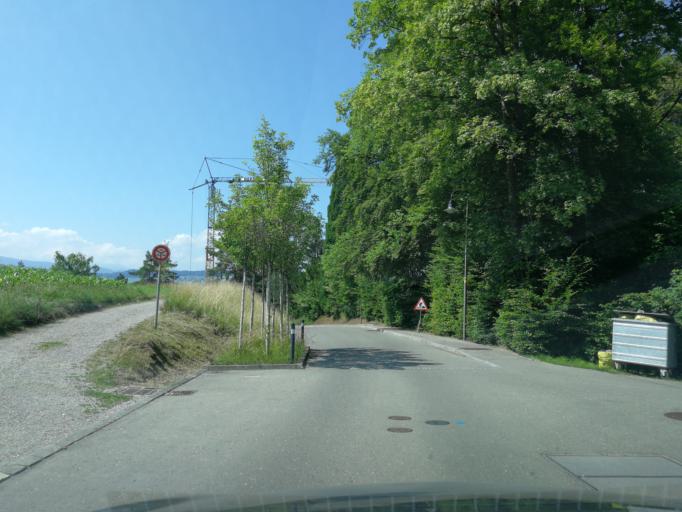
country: CH
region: Zurich
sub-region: Bezirk Meilen
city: Meilen
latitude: 47.2773
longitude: 8.6427
